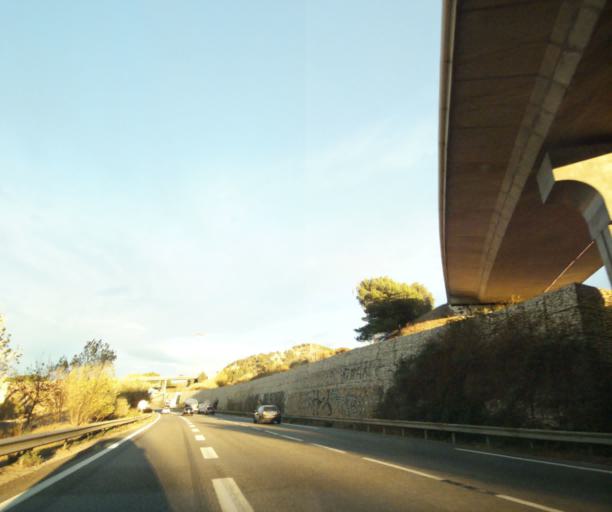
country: FR
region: Provence-Alpes-Cote d'Azur
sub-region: Departement des Bouches-du-Rhone
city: Les Pennes-Mirabeau
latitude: 43.3996
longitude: 5.2952
